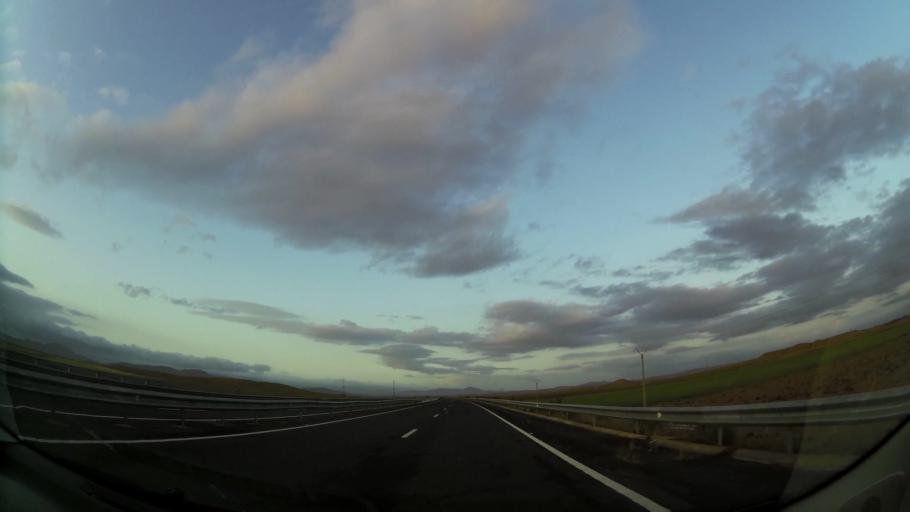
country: MA
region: Oriental
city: Taourirt
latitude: 34.5524
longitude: -2.8518
